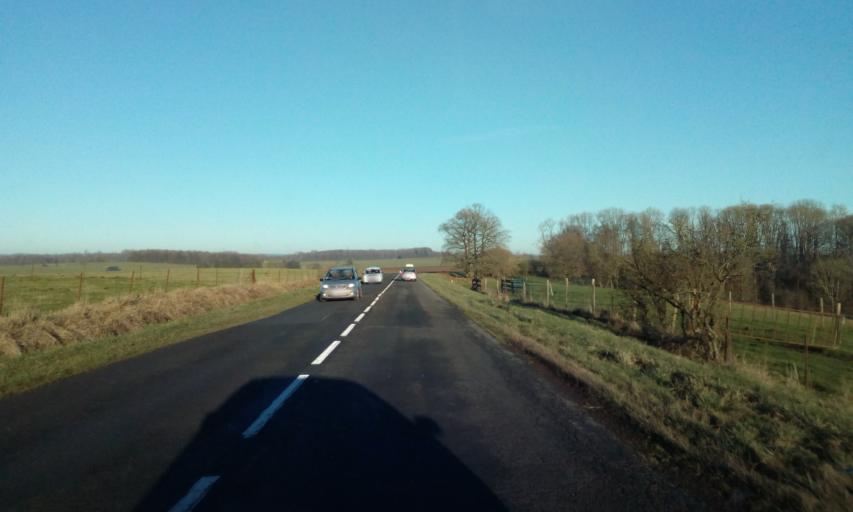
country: FR
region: Champagne-Ardenne
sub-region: Departement des Ardennes
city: Signy-le-Petit
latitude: 49.7797
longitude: 4.3638
